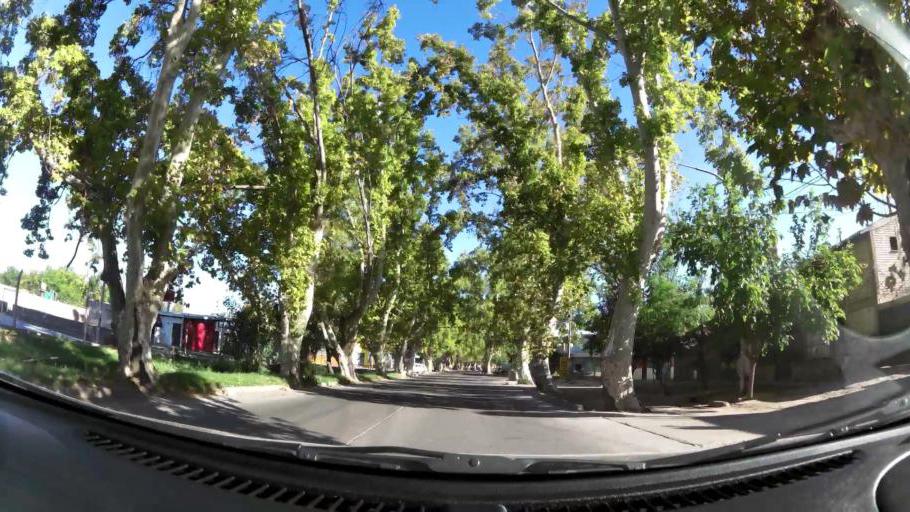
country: AR
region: Mendoza
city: Las Heras
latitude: -32.8516
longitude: -68.8270
